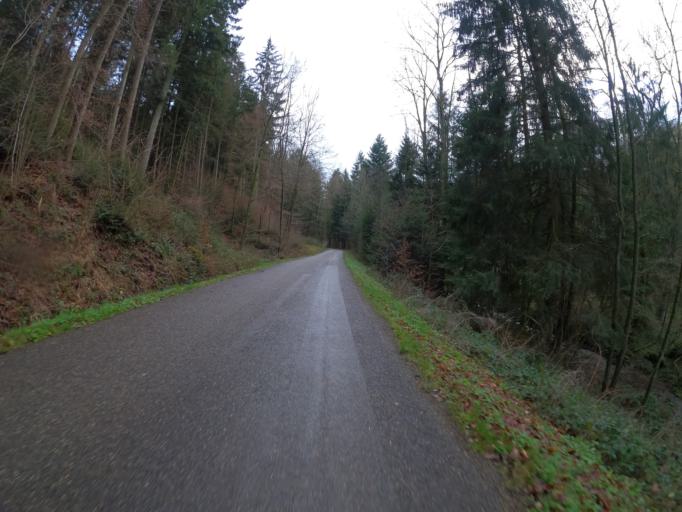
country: DE
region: Baden-Wuerttemberg
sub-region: Regierungsbezirk Stuttgart
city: Lorch
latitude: 48.7844
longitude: 9.7226
